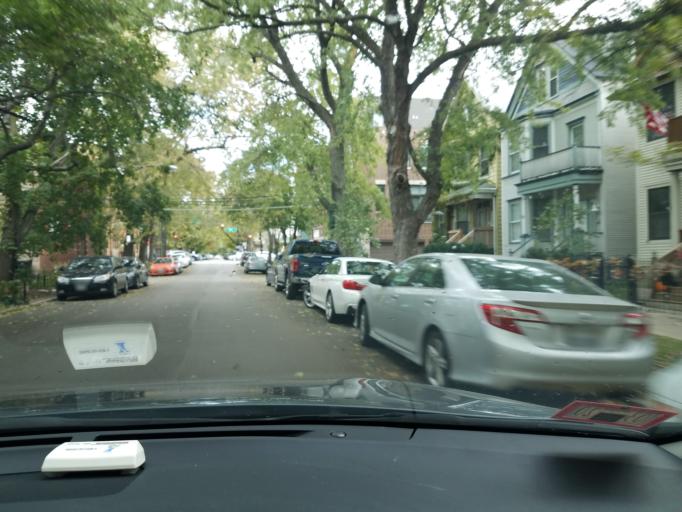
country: US
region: Illinois
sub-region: Cook County
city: Chicago
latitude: 41.9317
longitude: -87.6659
